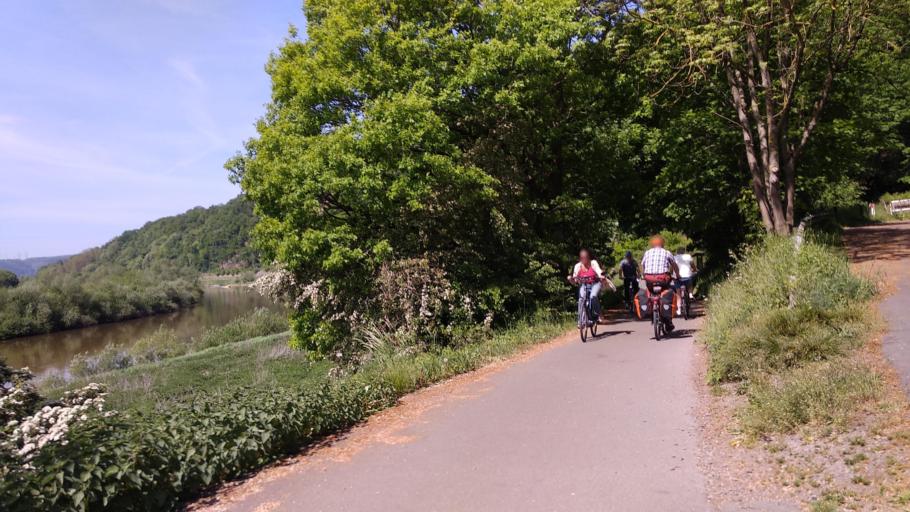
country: DE
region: Lower Saxony
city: Bad Karlshafen
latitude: 51.6486
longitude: 9.4384
